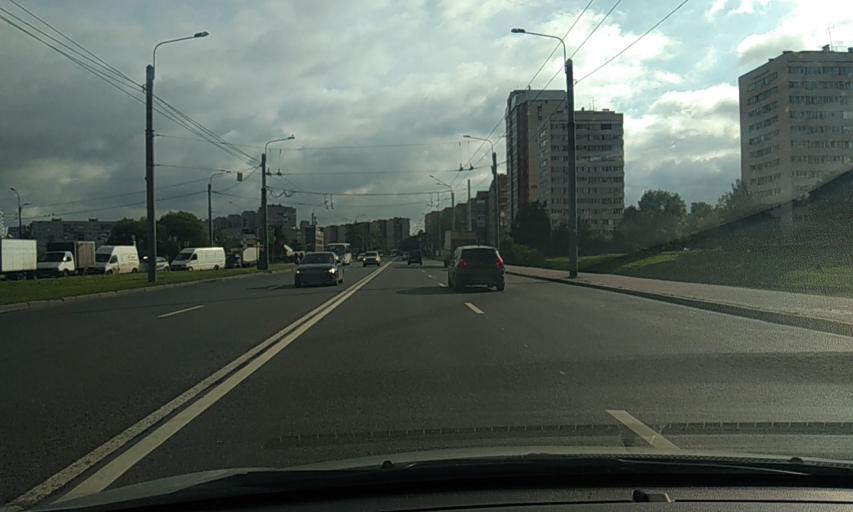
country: RU
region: St.-Petersburg
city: Uritsk
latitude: 59.8332
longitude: 30.2084
